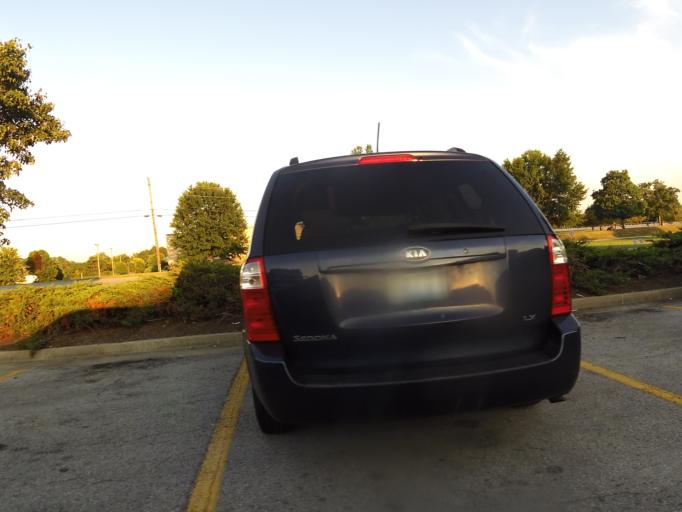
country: US
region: Kentucky
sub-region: Scott County
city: Georgetown
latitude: 38.2761
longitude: -84.5529
